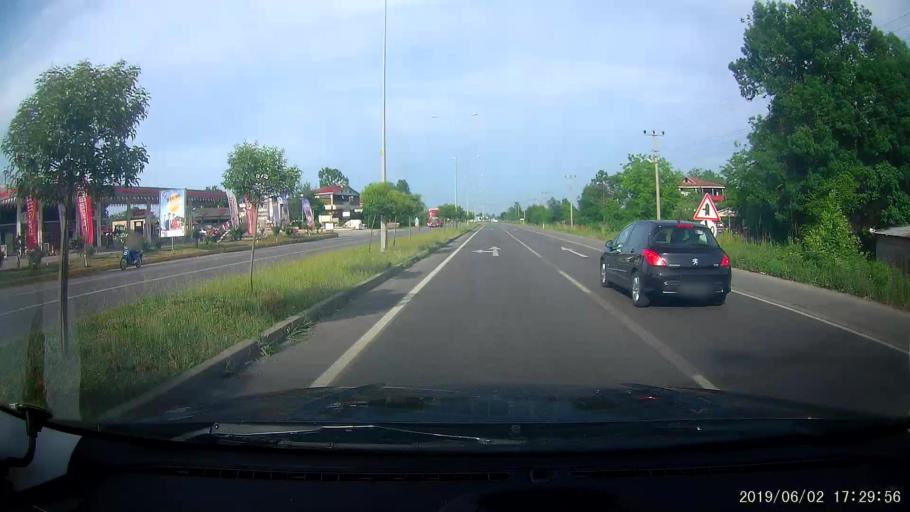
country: TR
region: Samsun
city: Carsamba
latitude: 41.2138
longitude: 36.7698
